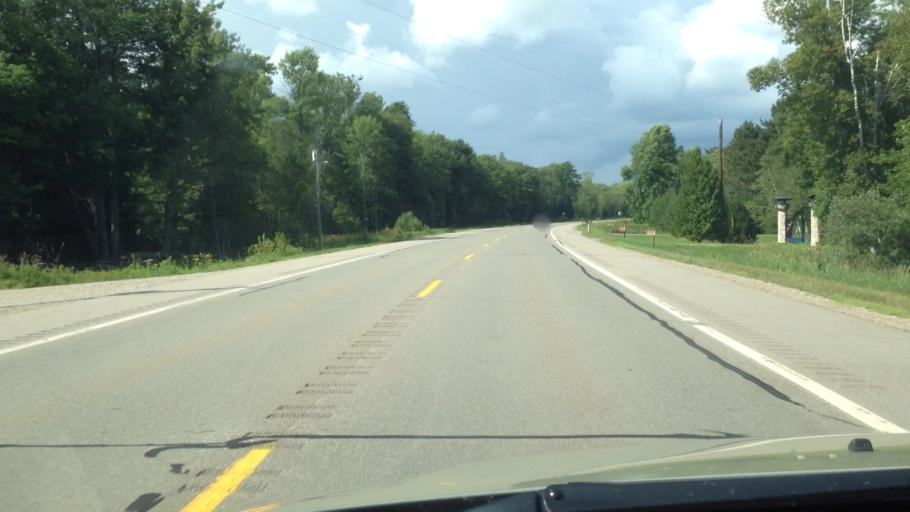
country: US
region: Michigan
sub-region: Menominee County
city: Menominee
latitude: 45.3034
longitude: -87.4396
